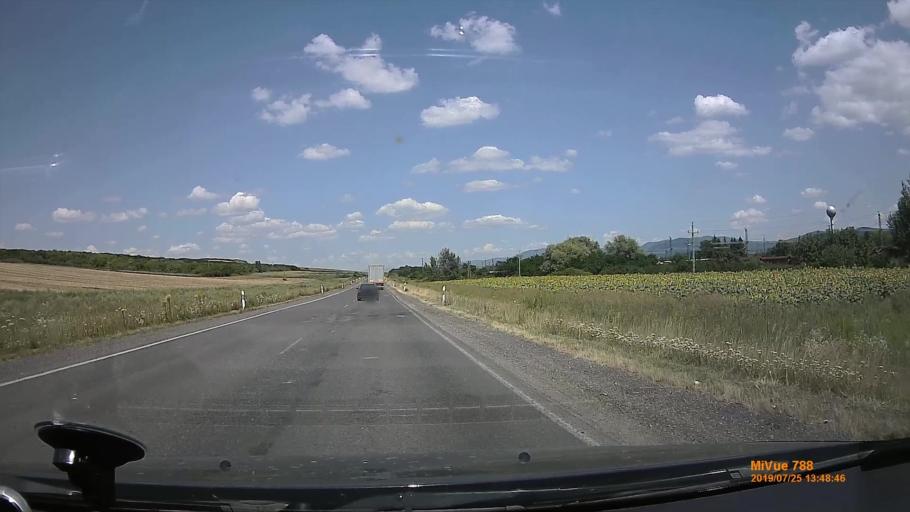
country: HU
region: Borsod-Abauj-Zemplen
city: Gonc
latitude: 48.5099
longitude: 21.2283
